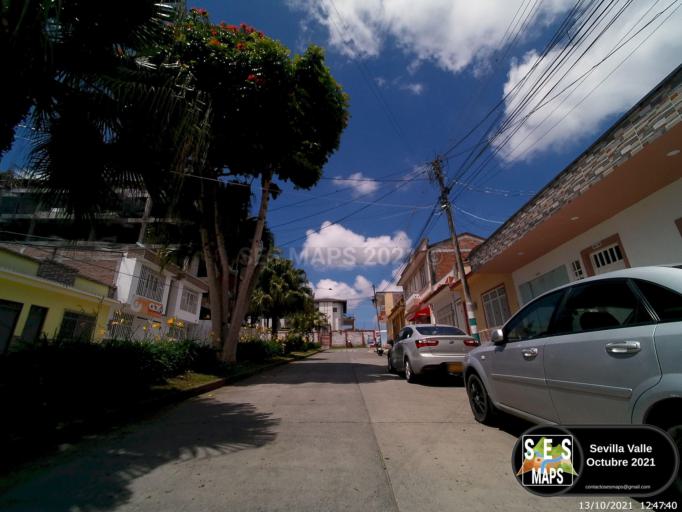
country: CO
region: Valle del Cauca
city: Sevilla
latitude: 4.2683
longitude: -75.9329
